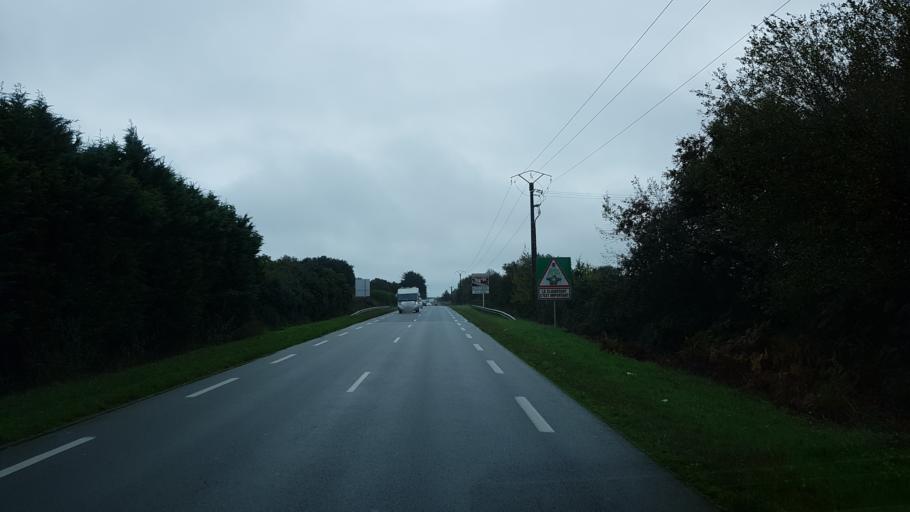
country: FR
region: Brittany
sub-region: Departement du Morbihan
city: Sarzeau
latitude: 47.5247
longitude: -2.7895
